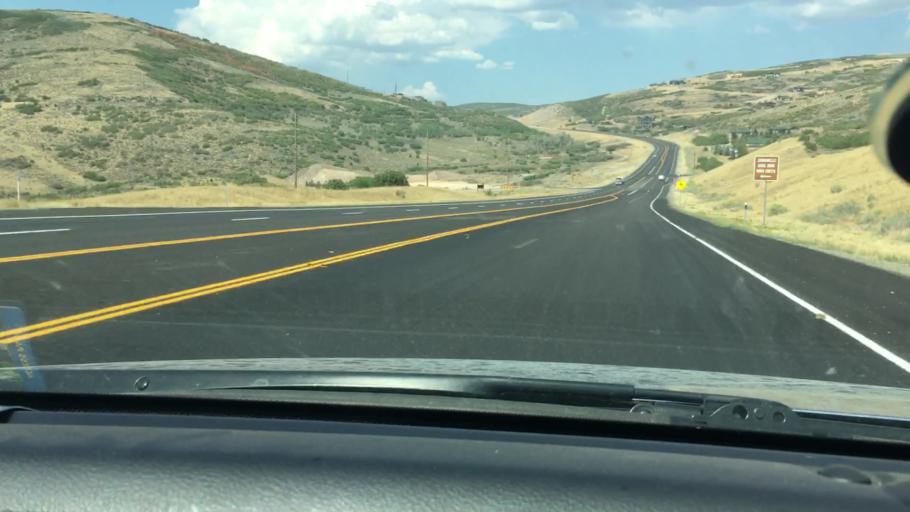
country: US
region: Utah
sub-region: Summit County
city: Park City
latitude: 40.6581
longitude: -111.4144
